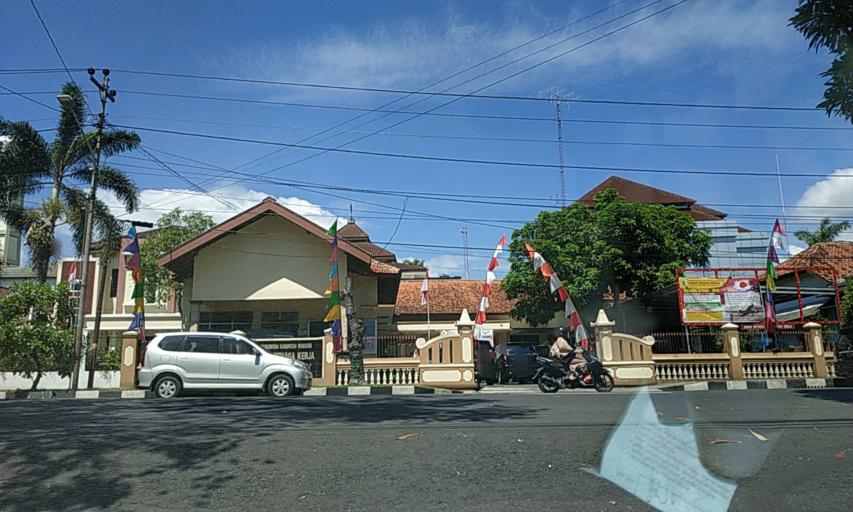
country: ID
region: Central Java
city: Selogiri
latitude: -7.8138
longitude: 110.9250
